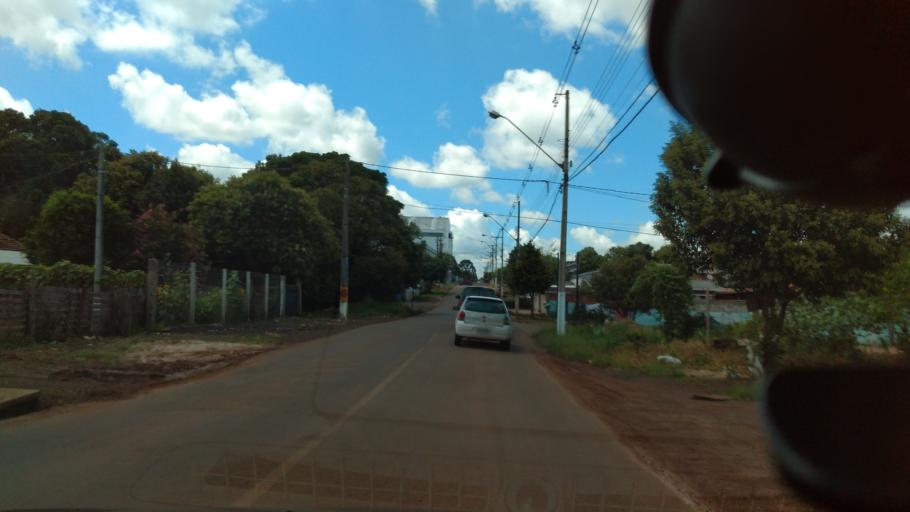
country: BR
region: Parana
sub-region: Guarapuava
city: Guarapuava
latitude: -25.3952
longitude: -51.4989
